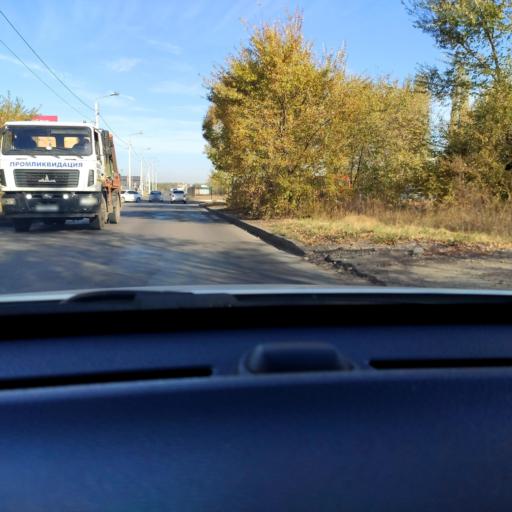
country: RU
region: Voronezj
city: Somovo
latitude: 51.6758
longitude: 39.2914
